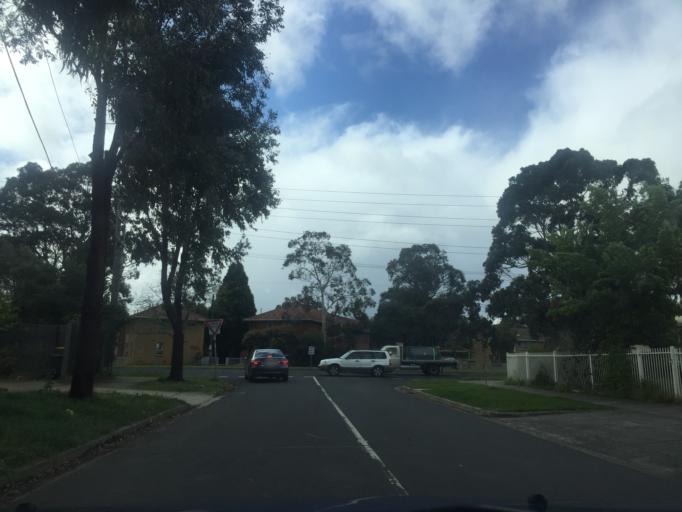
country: AU
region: Victoria
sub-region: Banyule
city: Bellfield
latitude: -37.7498
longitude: 145.0379
